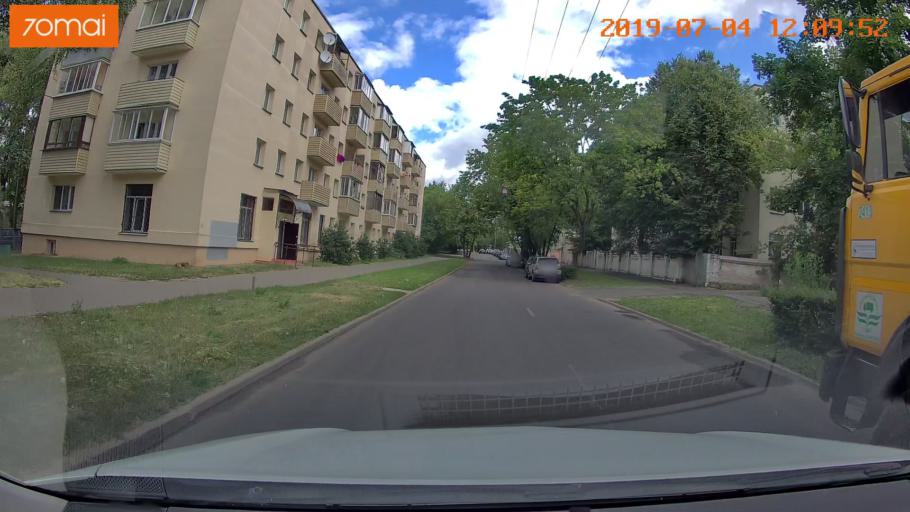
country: BY
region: Minsk
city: Minsk
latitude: 53.9299
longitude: 27.6056
